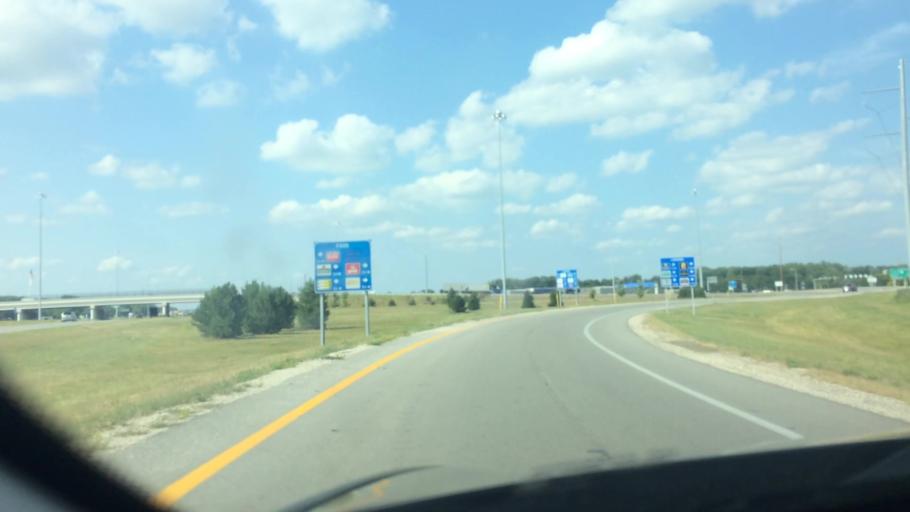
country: US
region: Ohio
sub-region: Lucas County
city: Maumee
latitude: 41.5782
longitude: -83.6906
